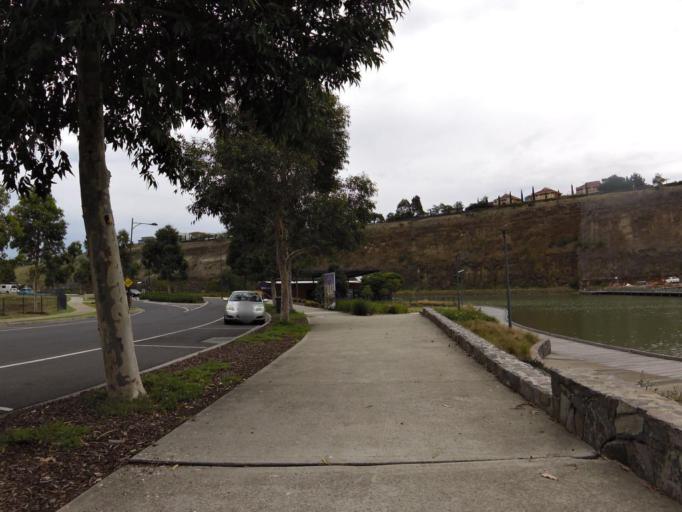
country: AU
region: Victoria
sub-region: Moonee Valley
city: Keilor East
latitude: -37.7373
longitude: 144.8758
